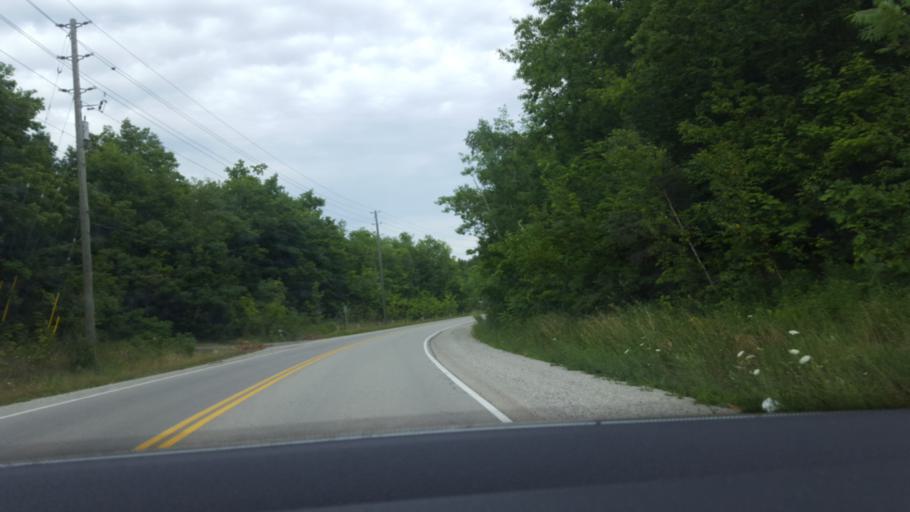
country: CA
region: Ontario
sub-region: Halton
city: Milton
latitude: 43.4980
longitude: -79.9871
